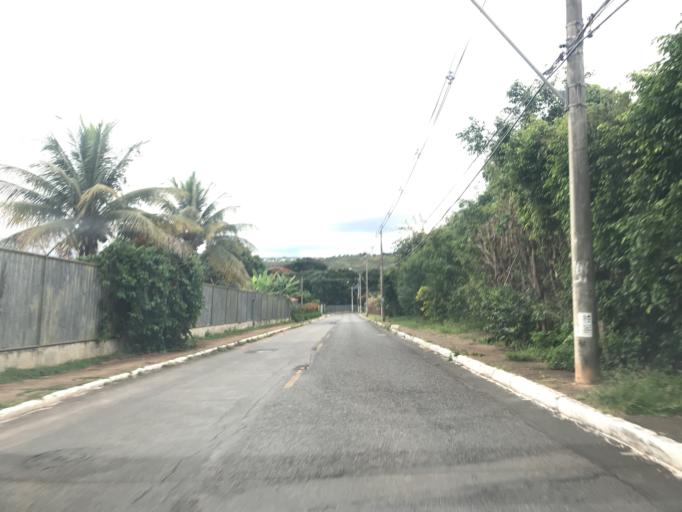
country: BR
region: Federal District
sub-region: Brasilia
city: Brasilia
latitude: -15.7211
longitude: -47.8767
